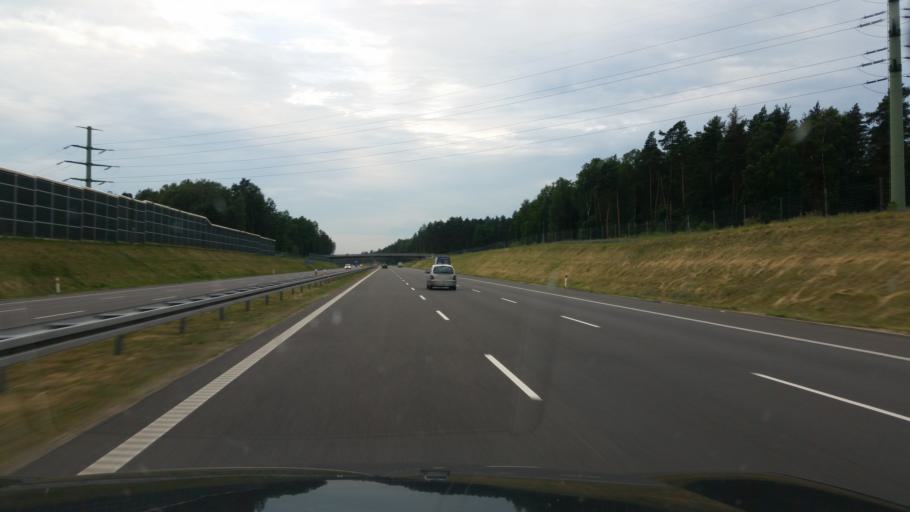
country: PL
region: Silesian Voivodeship
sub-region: Powiat rybnicki
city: Stanowice
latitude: 50.1085
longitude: 18.6733
